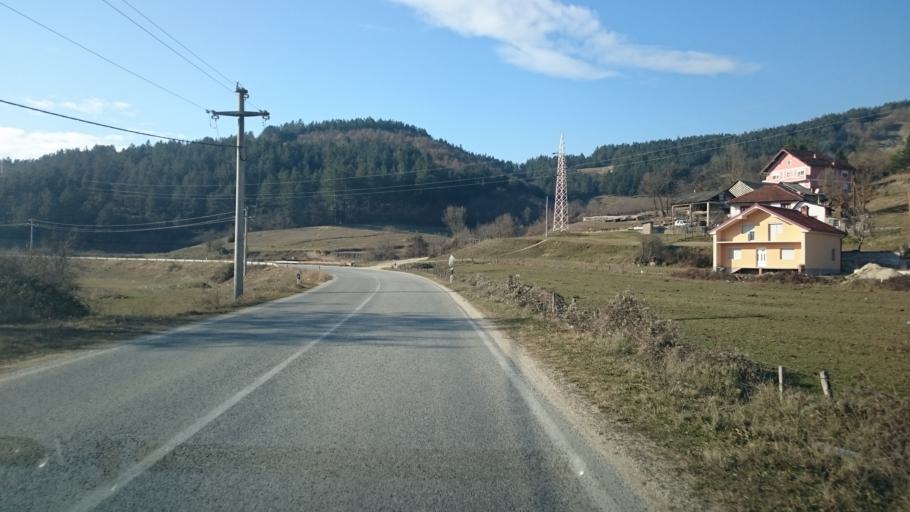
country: MK
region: Plasnica
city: Plasnica
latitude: 41.4840
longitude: 21.1095
